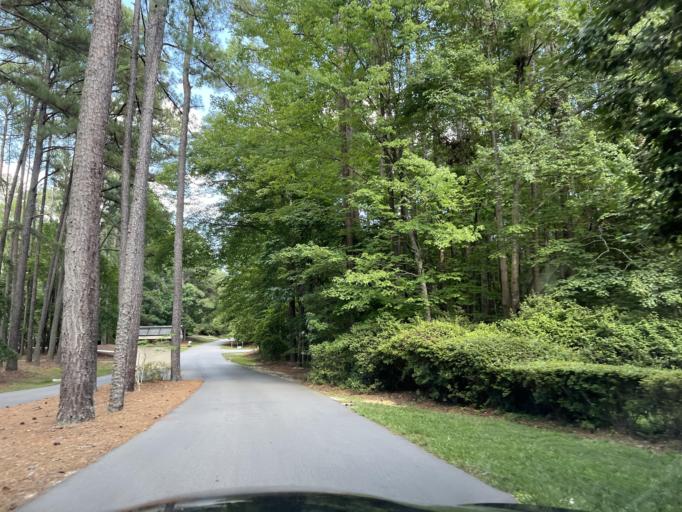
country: US
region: North Carolina
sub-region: Wake County
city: Wake Forest
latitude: 35.9388
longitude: -78.6442
